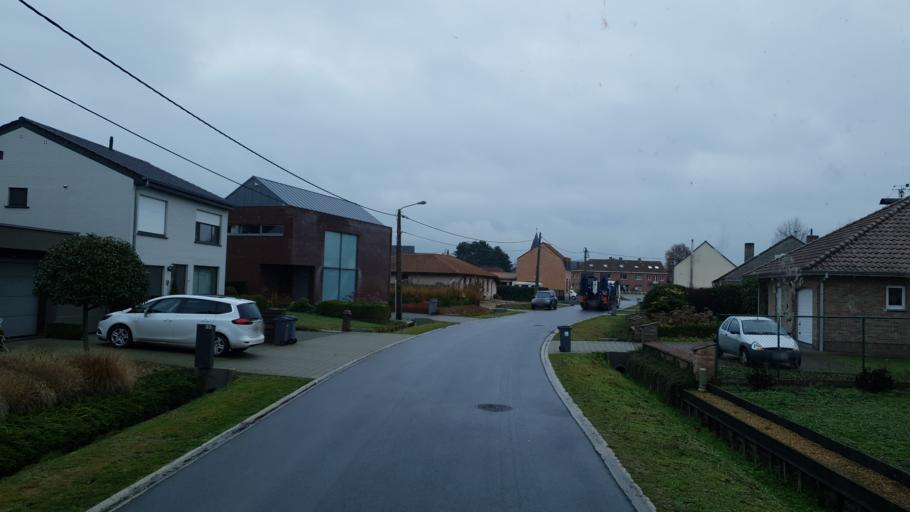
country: BE
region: Flanders
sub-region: Provincie Antwerpen
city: Olen
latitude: 51.1887
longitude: 4.9045
